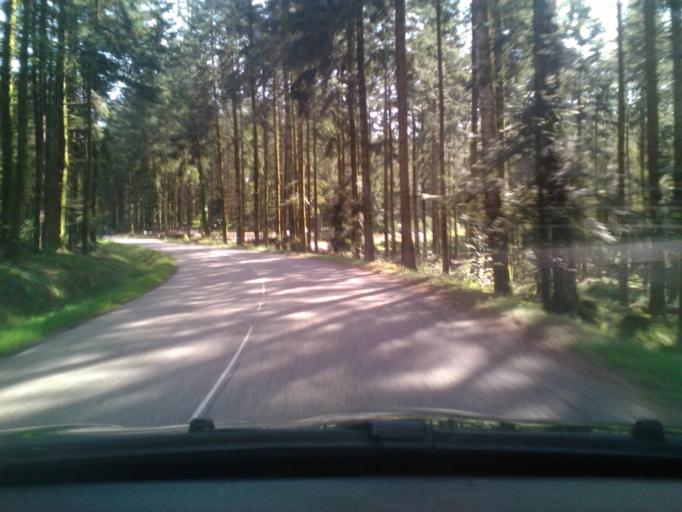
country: FR
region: Lorraine
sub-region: Departement des Vosges
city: Bruyeres
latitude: 48.2786
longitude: 6.7830
